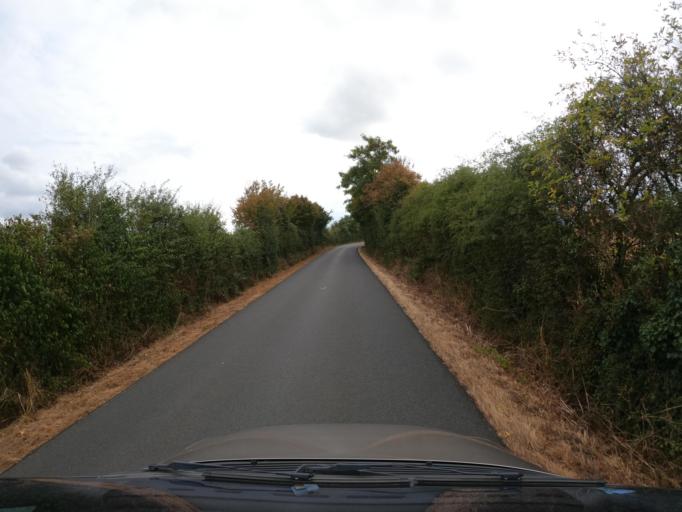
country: FR
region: Pays de la Loire
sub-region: Departement de Maine-et-Loire
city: Saint-Christophe-du-Bois
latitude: 47.0397
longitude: -0.9327
